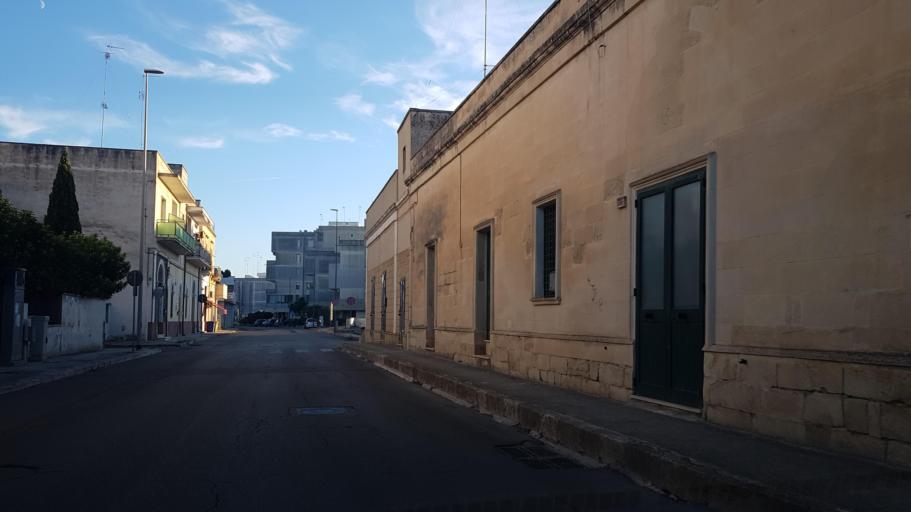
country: IT
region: Apulia
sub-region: Provincia di Lecce
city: Lecce
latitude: 40.3643
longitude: 18.1767
